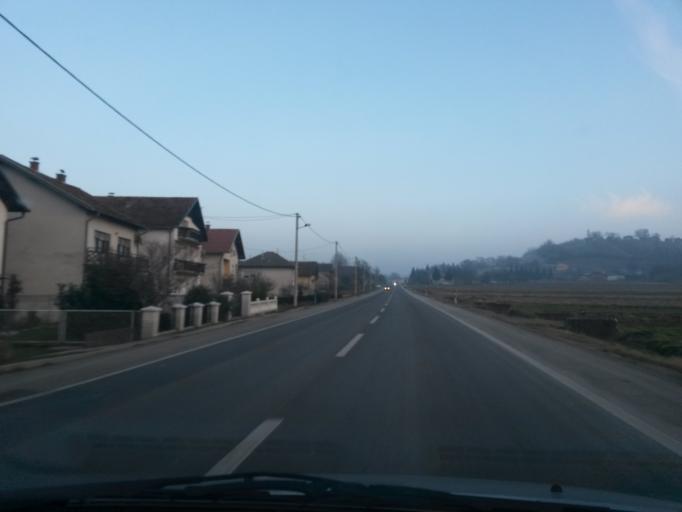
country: HR
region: Varazdinska
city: Ludbreg
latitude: 46.2395
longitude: 16.6342
